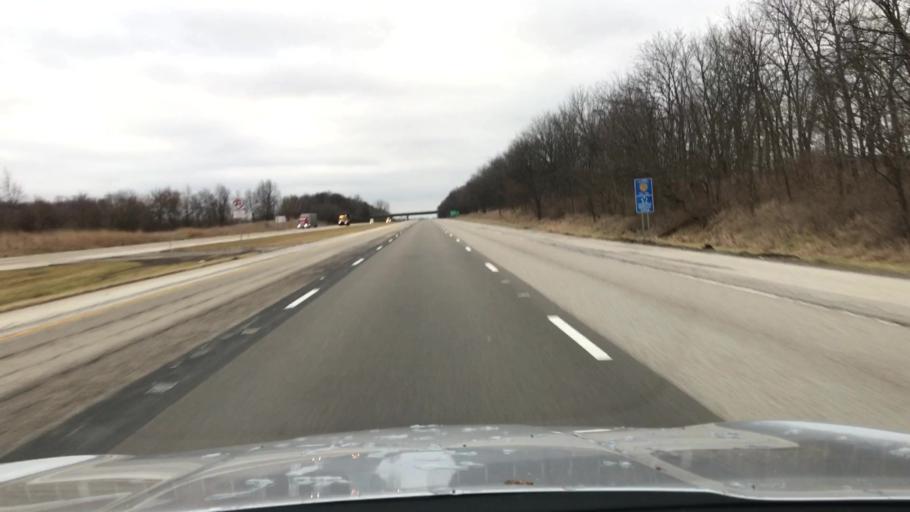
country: US
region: Illinois
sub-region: Logan County
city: Lincoln
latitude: 40.1532
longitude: -89.4176
